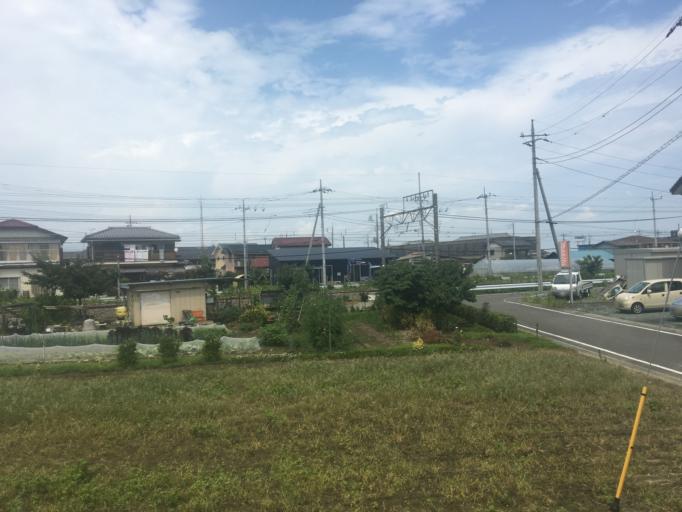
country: JP
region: Gunma
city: Fujioka
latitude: 36.2821
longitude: 139.0816
